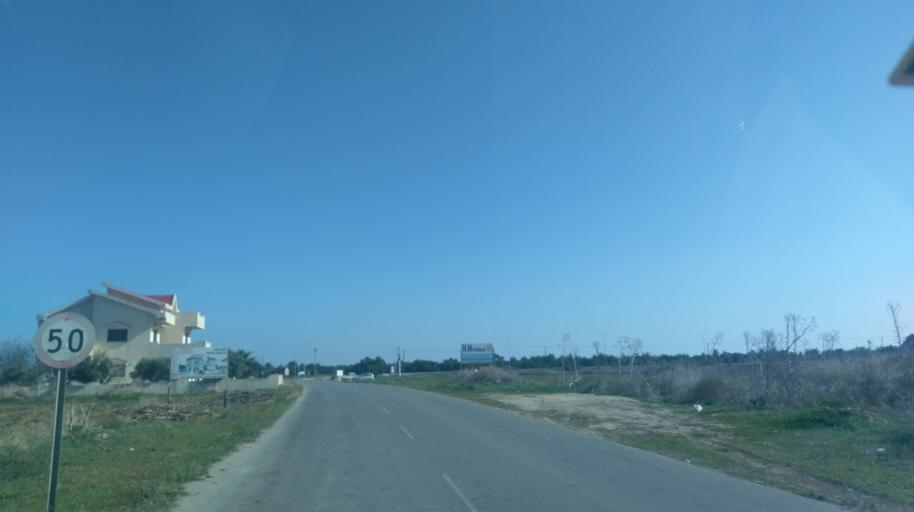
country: CY
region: Ammochostos
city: Trikomo
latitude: 35.2304
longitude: 33.8950
